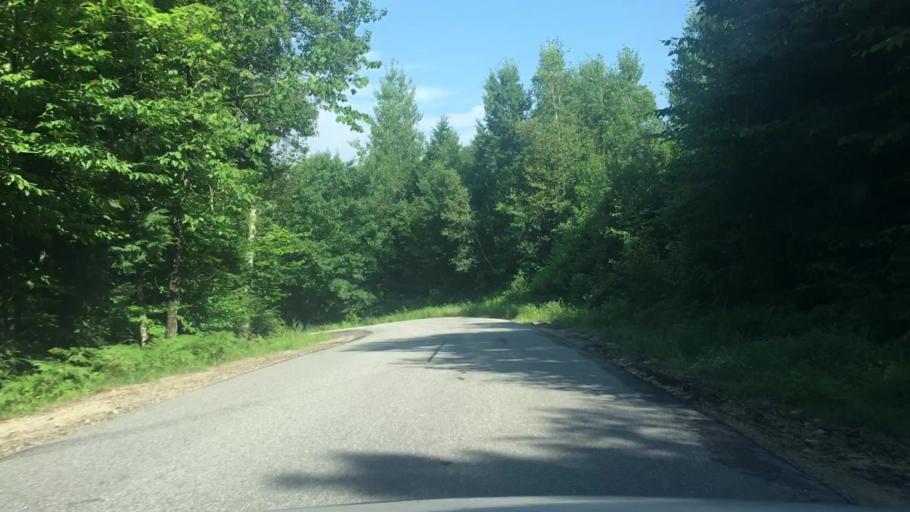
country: US
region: Maine
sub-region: Oxford County
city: West Paris
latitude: 44.3290
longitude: -70.5136
